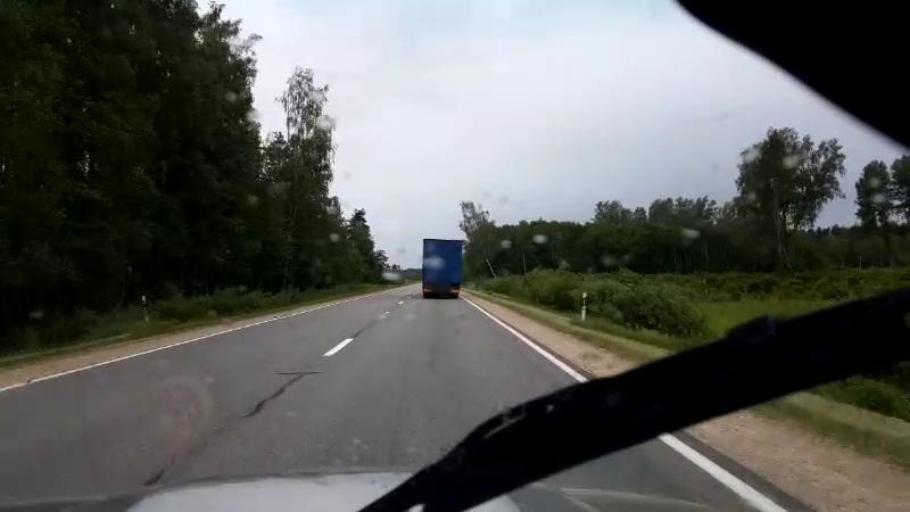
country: LV
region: Salaspils
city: Salaspils
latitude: 56.8872
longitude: 24.4074
